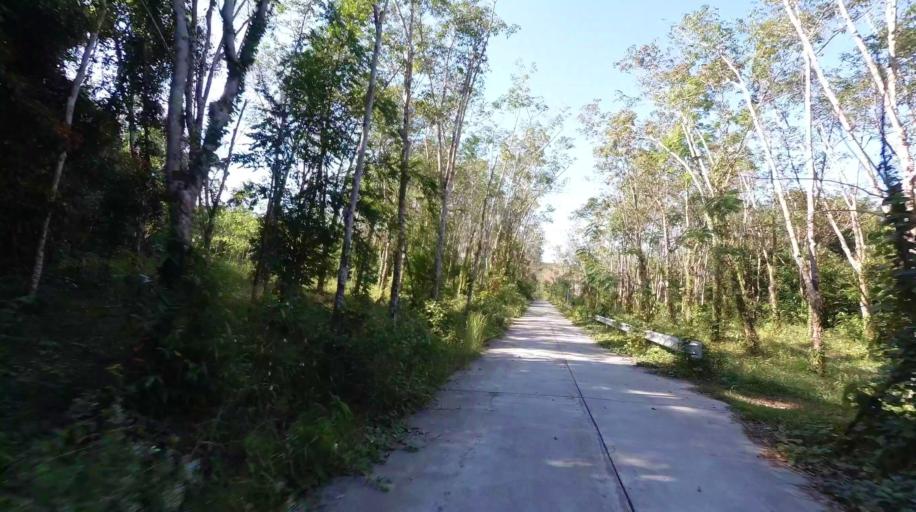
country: TH
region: Trat
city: Ko Kut
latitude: 11.6250
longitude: 102.5551
